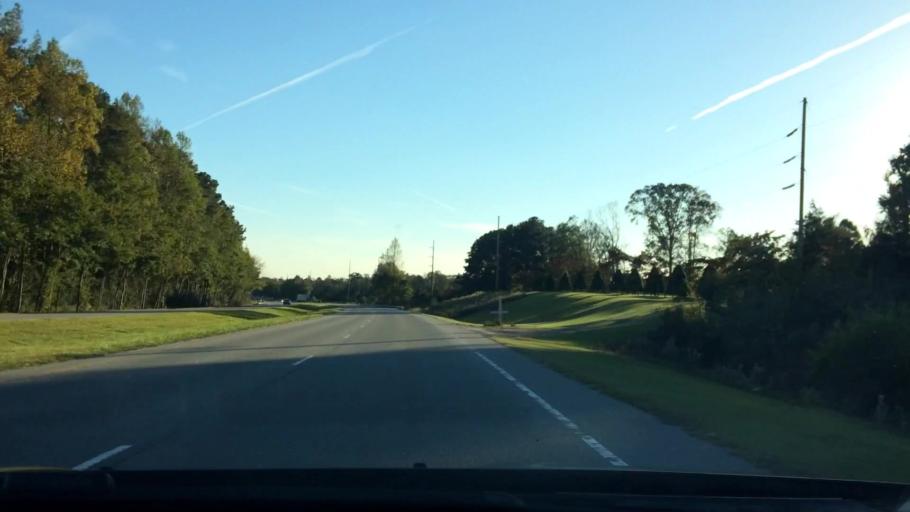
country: US
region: North Carolina
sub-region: Pitt County
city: Grifton
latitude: 35.3950
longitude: -77.4440
